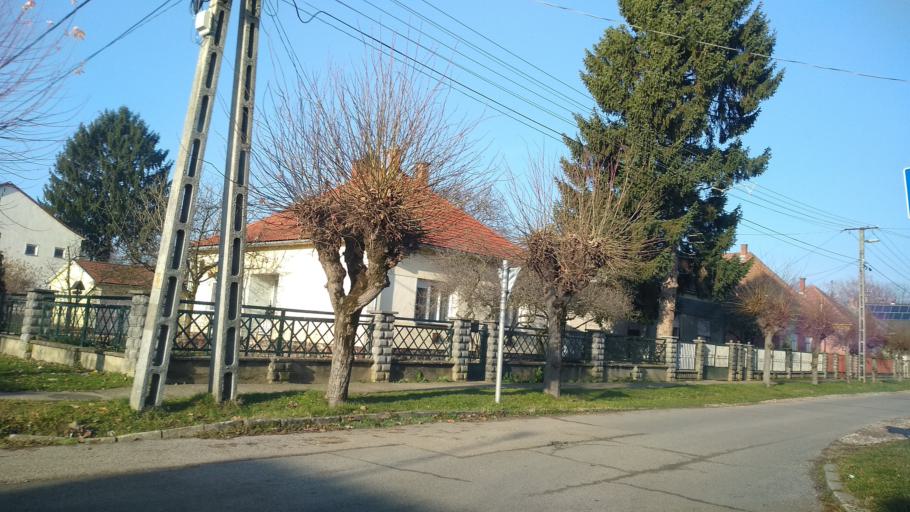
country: HU
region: Somogy
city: Barcs
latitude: 45.9598
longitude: 17.4548
